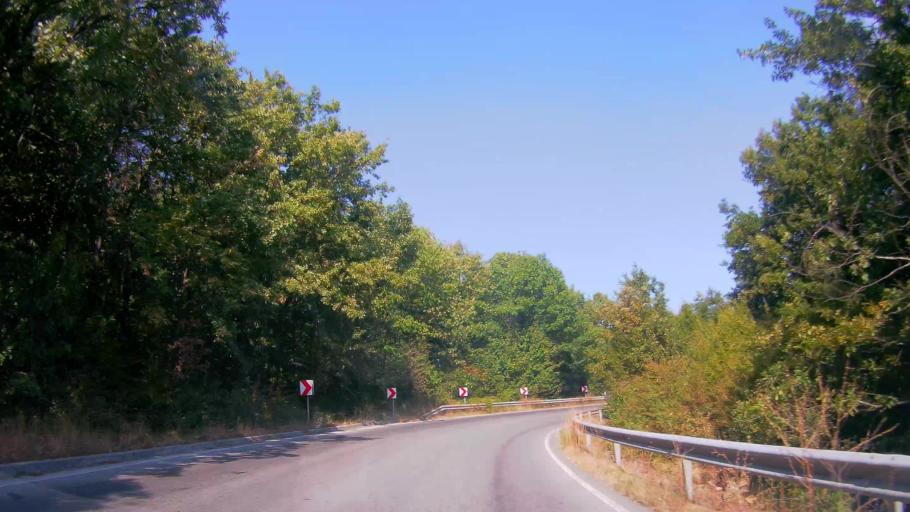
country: BG
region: Burgas
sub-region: Obshtina Sungurlare
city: Sungurlare
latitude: 42.8603
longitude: 26.9459
